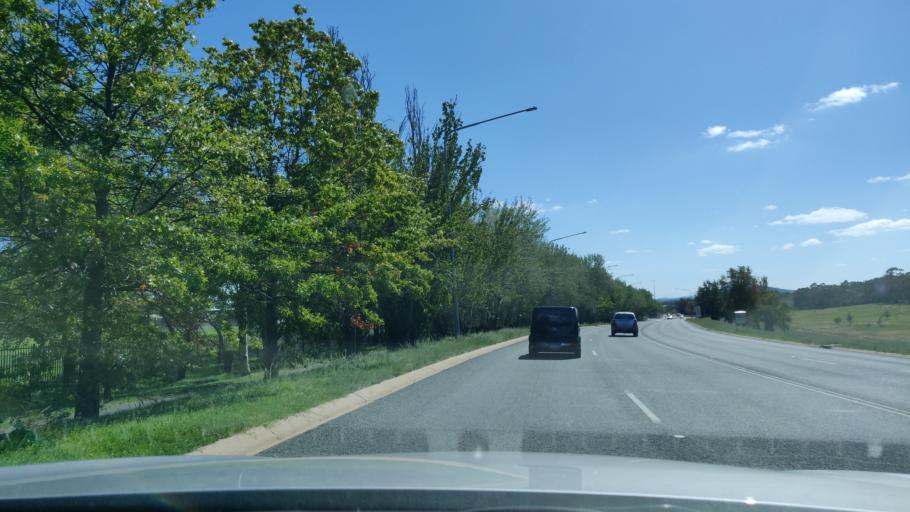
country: AU
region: Australian Capital Territory
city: Forrest
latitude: -35.3607
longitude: 149.0917
